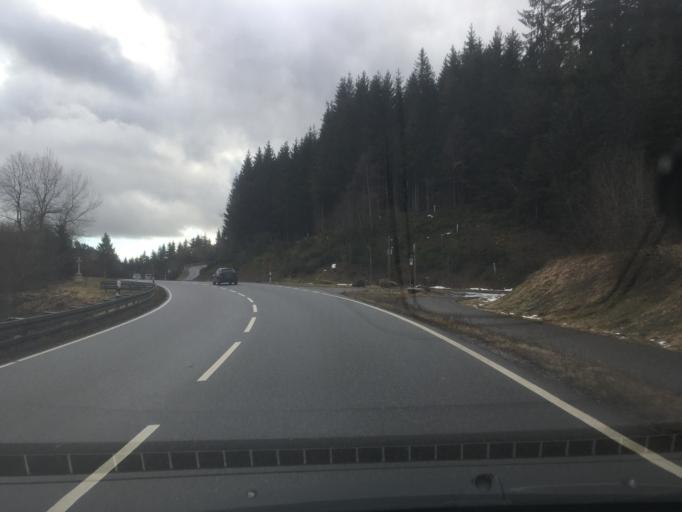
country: DE
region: Baden-Wuerttemberg
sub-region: Freiburg Region
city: Hausern
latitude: 47.7665
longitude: 8.1826
